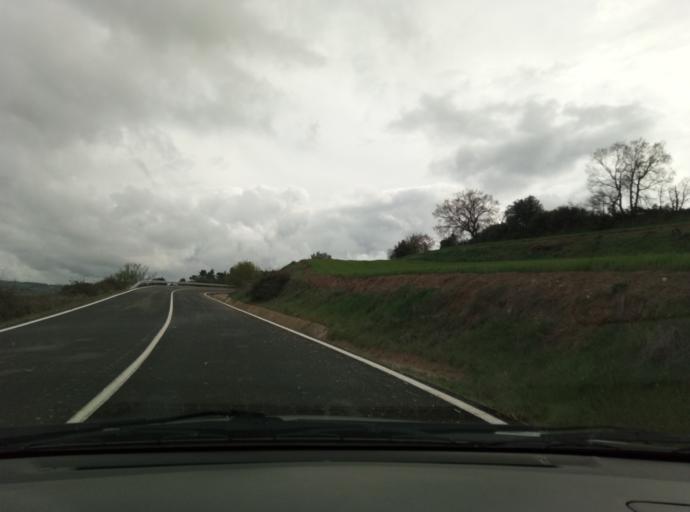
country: ES
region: Catalonia
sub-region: Provincia de Tarragona
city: Santa Coloma de Queralt
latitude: 41.5941
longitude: 1.3429
